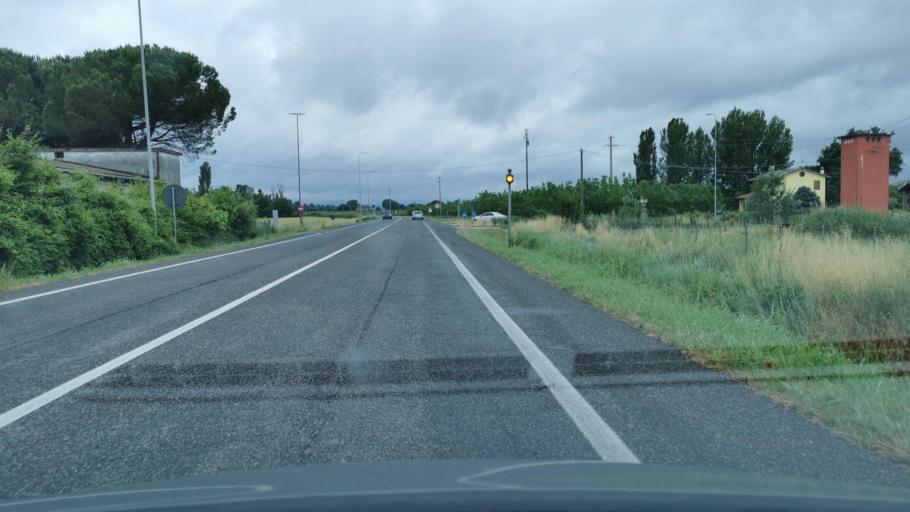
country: IT
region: Emilia-Romagna
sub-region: Provincia di Ravenna
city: Granarolo
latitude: 44.3564
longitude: 11.9292
